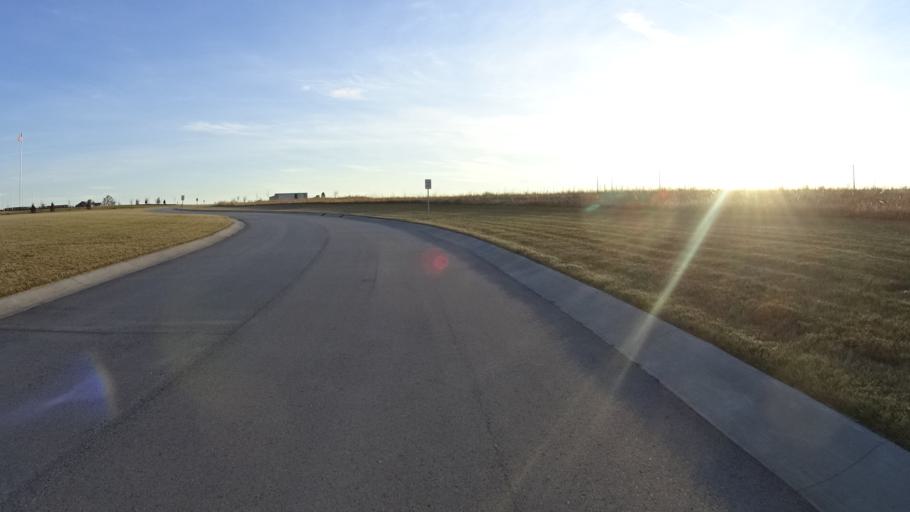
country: US
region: Nebraska
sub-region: Sarpy County
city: Chalco
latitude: 41.1390
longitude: -96.1341
